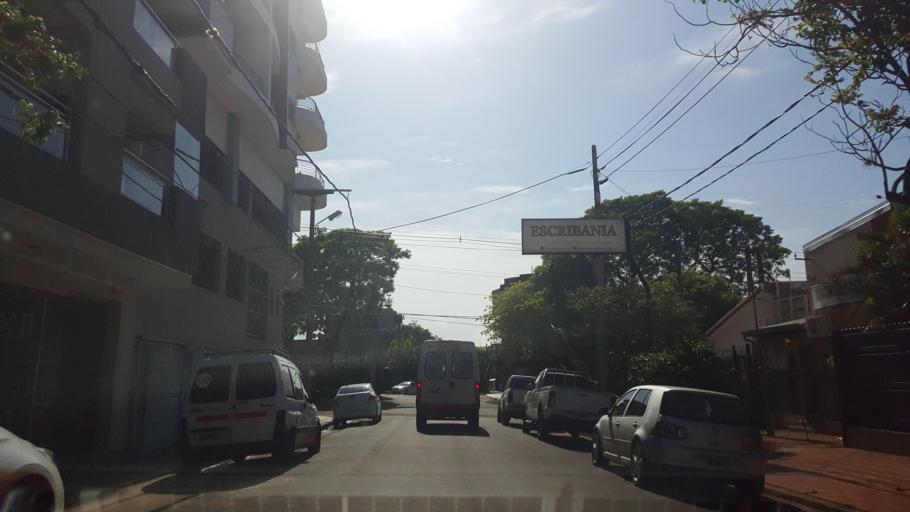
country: AR
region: Misiones
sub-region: Departamento de Capital
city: Posadas
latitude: -27.3742
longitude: -55.8887
